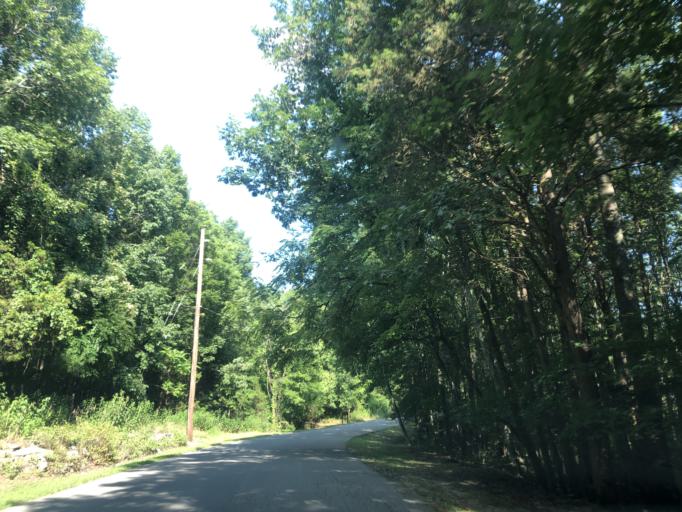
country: US
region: Tennessee
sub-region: Wilson County
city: Green Hill
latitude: 36.1374
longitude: -86.5973
